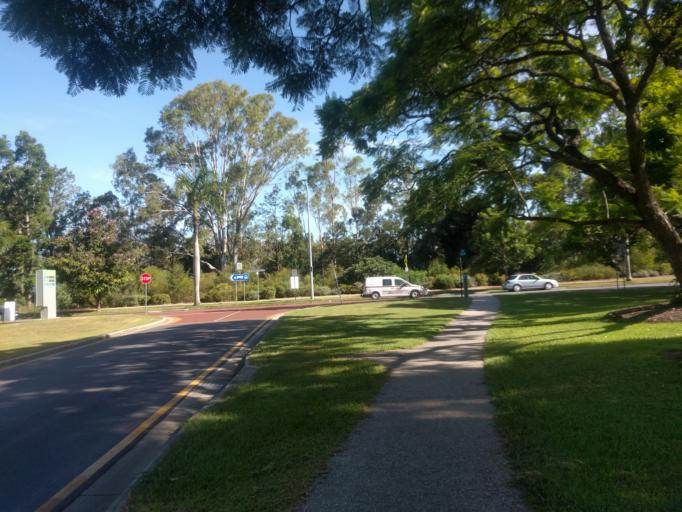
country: AU
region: Queensland
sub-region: Brisbane
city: Yeronga
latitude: -27.5012
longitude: 153.0182
